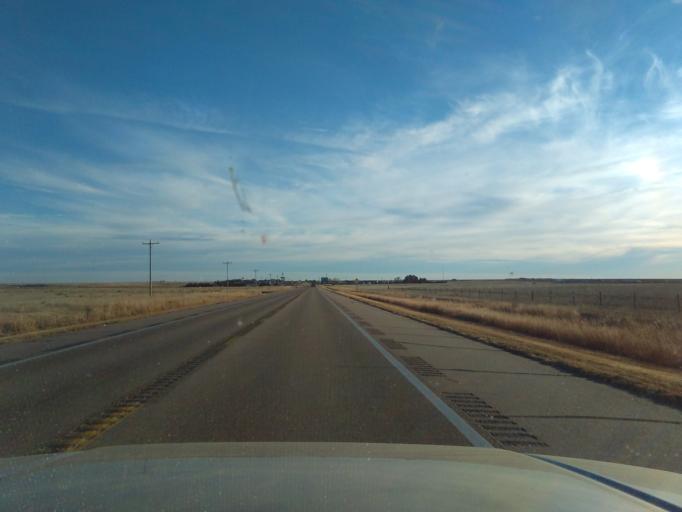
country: US
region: Kansas
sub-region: Logan County
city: Oakley
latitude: 39.2001
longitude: -100.8701
